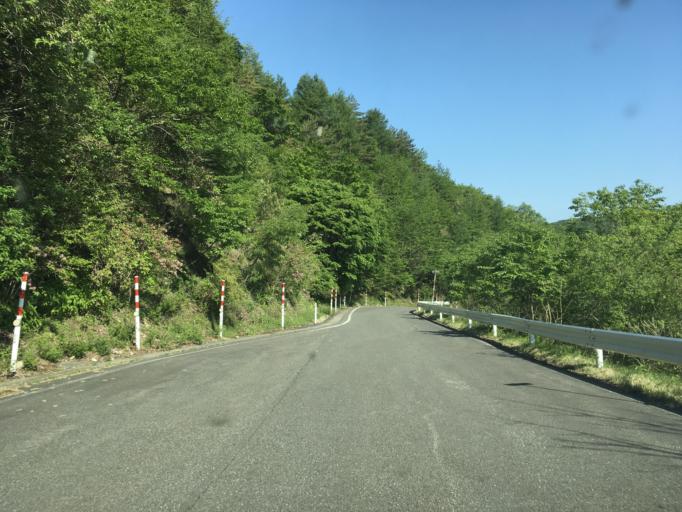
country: JP
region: Iwate
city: Ofunato
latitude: 39.1849
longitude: 141.7500
